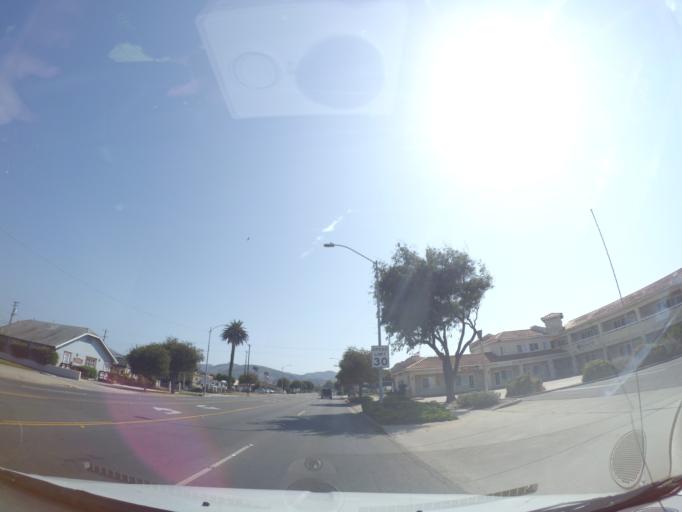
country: US
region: California
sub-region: Santa Barbara County
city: Lompoc
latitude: 34.6462
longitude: -120.4579
